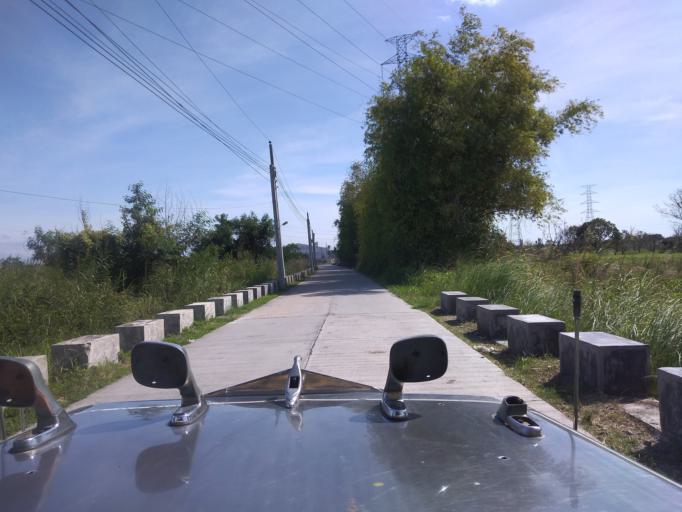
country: PH
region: Central Luzon
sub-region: Province of Pampanga
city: San Juan
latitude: 15.0245
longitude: 120.6670
